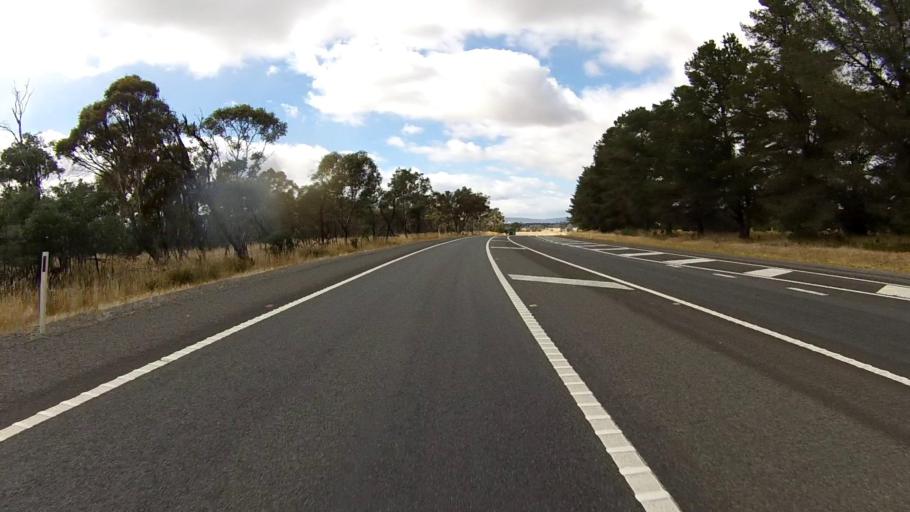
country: AU
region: Tasmania
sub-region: Northern Midlands
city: Evandale
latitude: -41.8296
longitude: 147.4410
